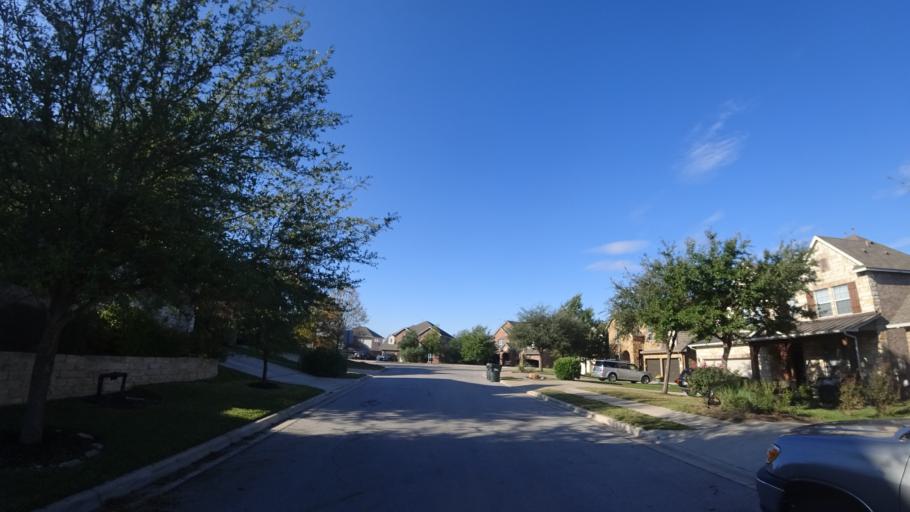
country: US
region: Texas
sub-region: Travis County
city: Hudson Bend
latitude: 30.3661
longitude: -97.8985
